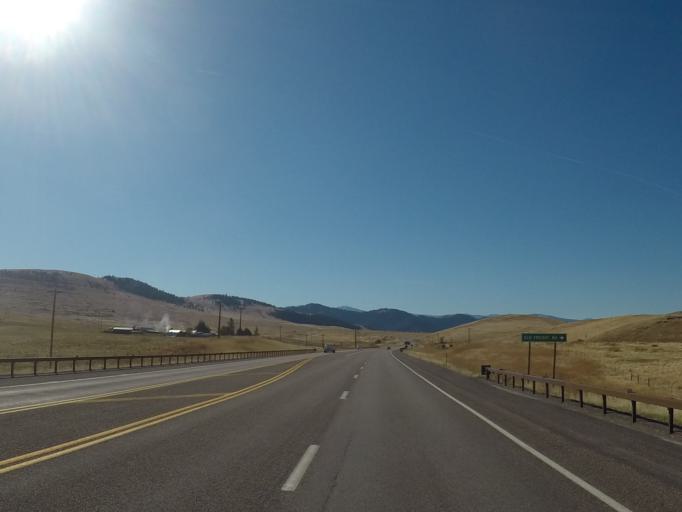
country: US
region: Montana
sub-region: Lake County
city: Ronan
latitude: 47.3024
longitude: -114.1333
